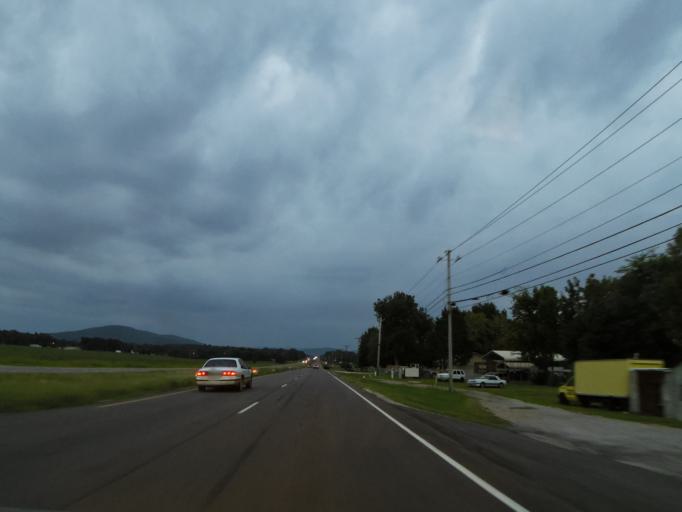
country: US
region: Alabama
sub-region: Madison County
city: Moores Mill
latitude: 34.7585
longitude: -86.4742
